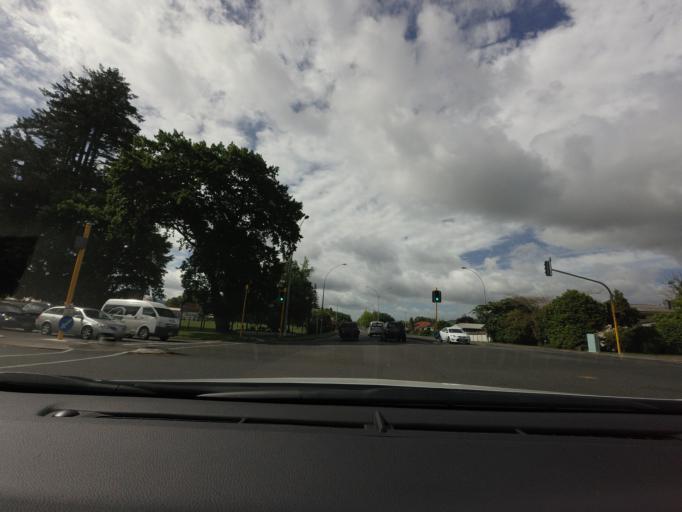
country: NZ
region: Bay of Plenty
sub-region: Rotorua District
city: Rotorua
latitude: -38.1368
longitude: 176.2354
